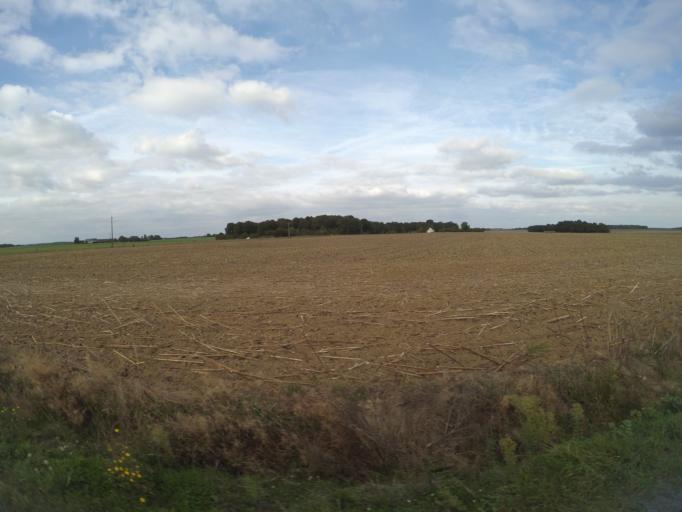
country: FR
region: Centre
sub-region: Departement d'Indre-et-Loire
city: Reugny
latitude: 47.4722
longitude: 0.9085
